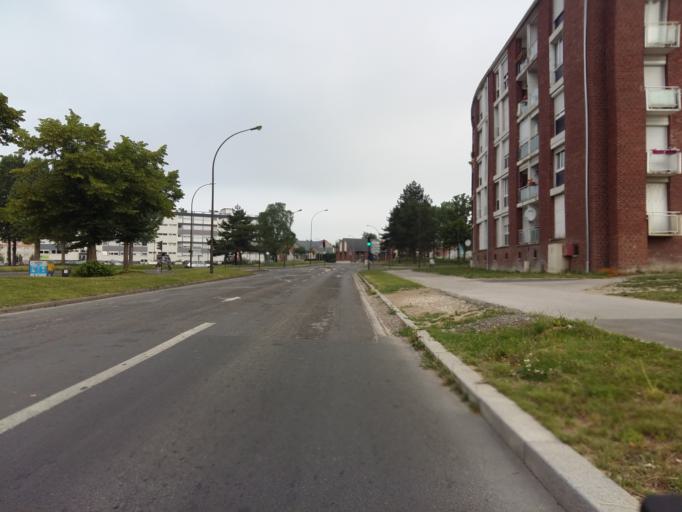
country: FR
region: Picardie
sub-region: Departement de la Somme
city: Amiens
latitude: 49.9079
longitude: 2.3013
